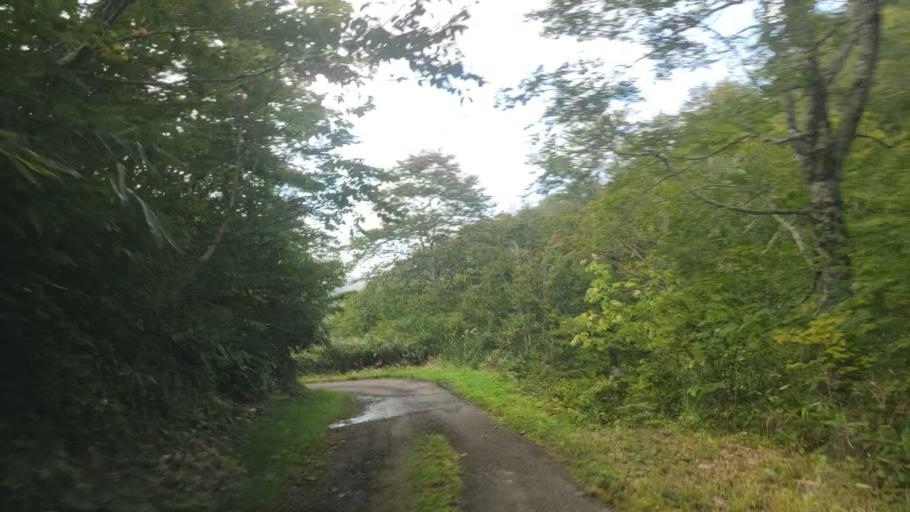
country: JP
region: Toyama
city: Yatsuomachi-higashikumisaka
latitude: 36.3514
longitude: 137.0641
